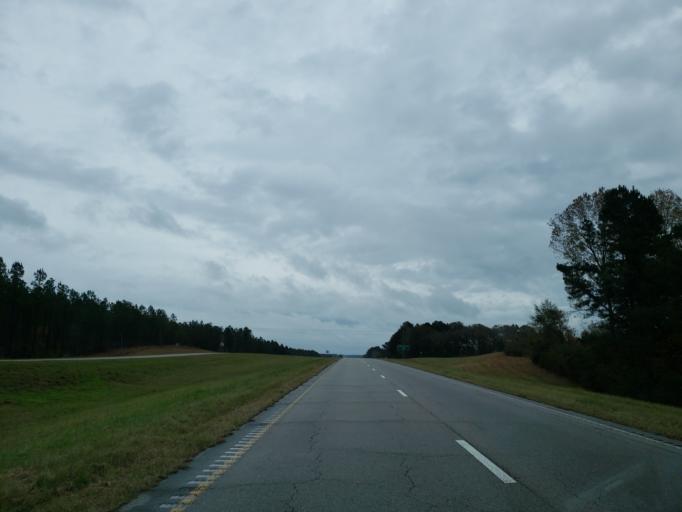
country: US
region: Mississippi
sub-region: Wayne County
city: Waynesboro
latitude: 31.6966
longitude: -88.8750
